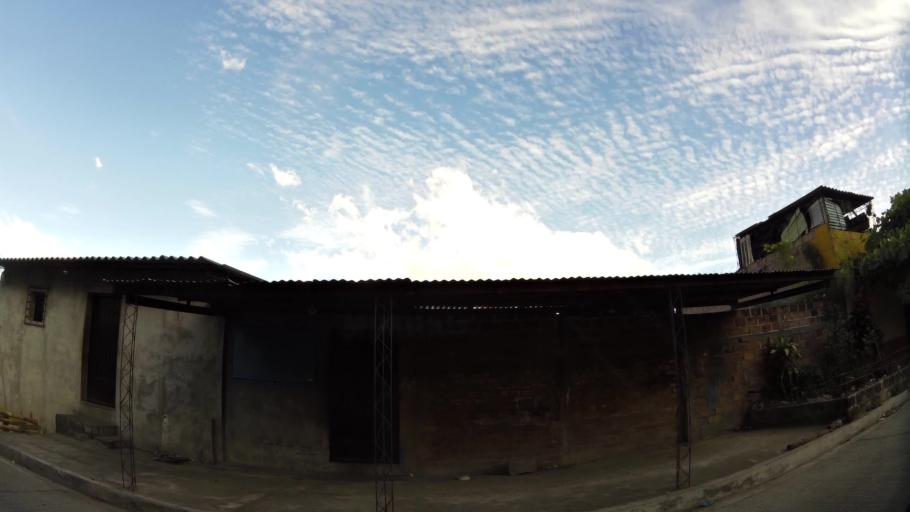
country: SV
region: Cuscatlan
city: Cojutepeque
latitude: 13.7160
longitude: -88.9331
